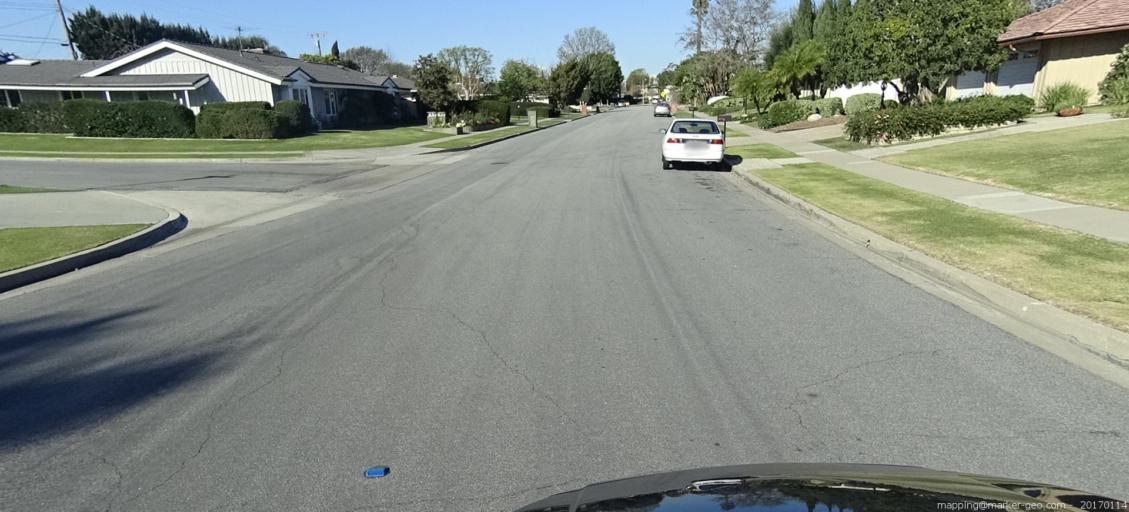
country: US
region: California
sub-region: Orange County
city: North Tustin
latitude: 33.7699
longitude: -117.8138
